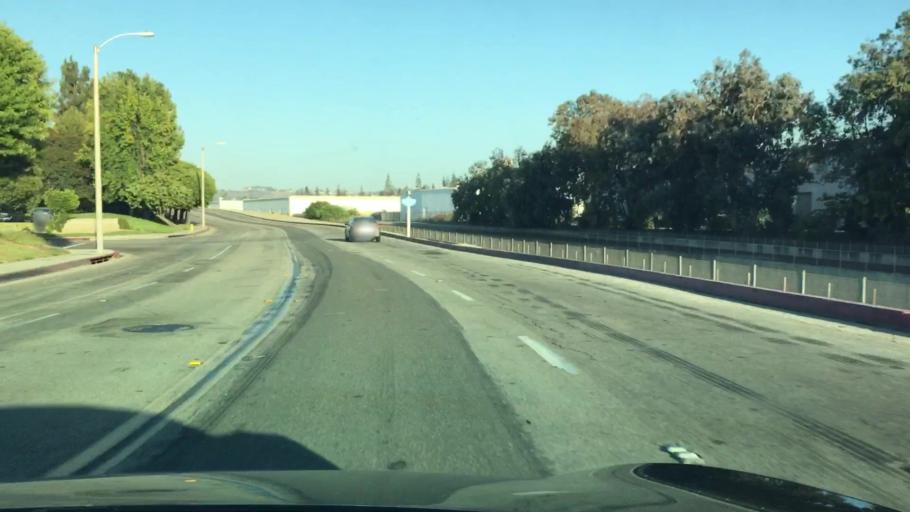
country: US
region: California
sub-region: Los Angeles County
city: South San Jose Hills
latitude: 34.0011
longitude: -117.8978
